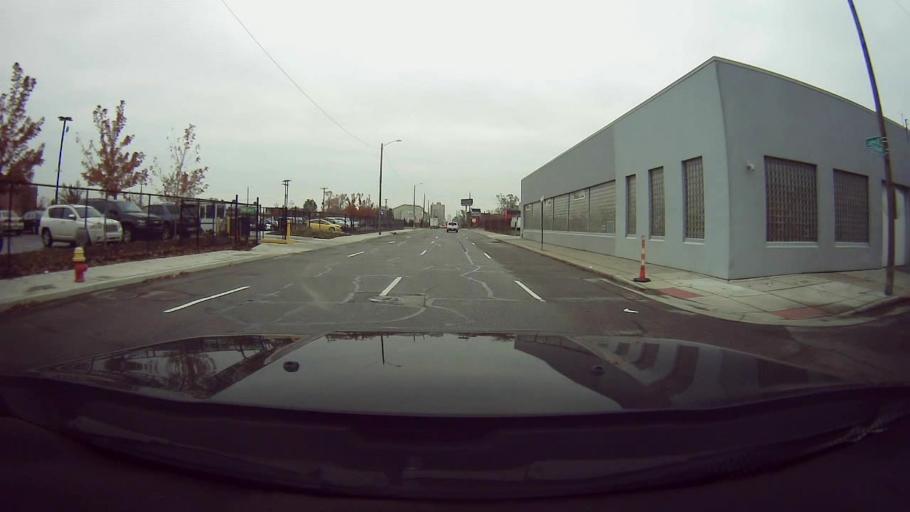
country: US
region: Michigan
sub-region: Wayne County
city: Hamtramck
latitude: 42.3682
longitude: -83.0692
